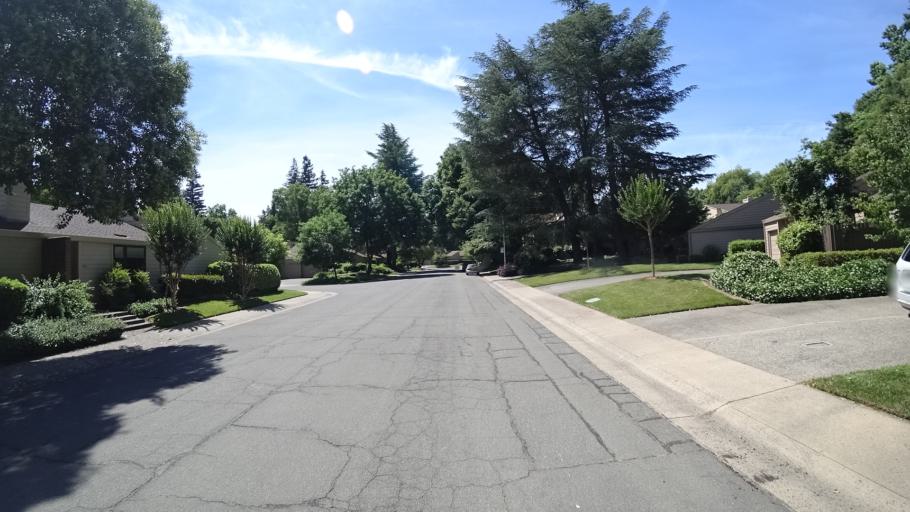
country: US
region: California
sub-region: Sacramento County
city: Arden-Arcade
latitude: 38.5672
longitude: -121.4145
